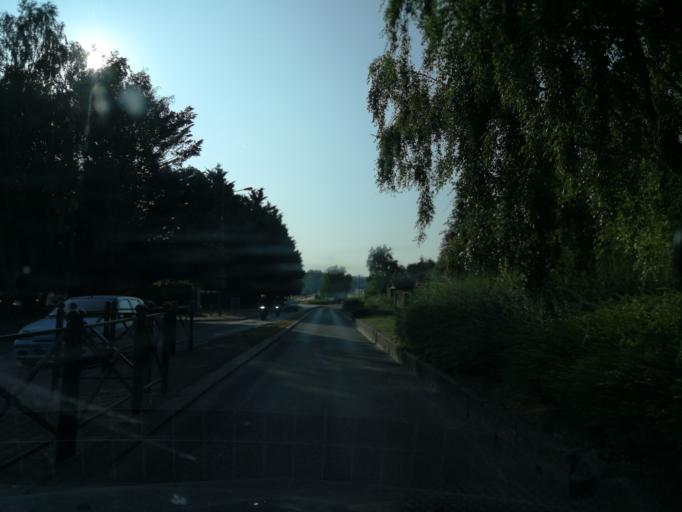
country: FR
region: Ile-de-France
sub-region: Departement de l'Essonne
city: Limours
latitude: 48.6420
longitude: 2.0896
